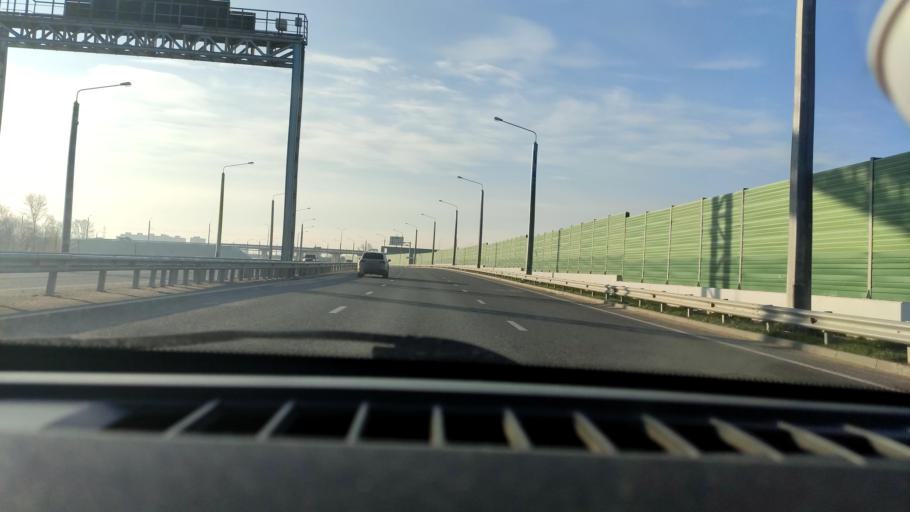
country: RU
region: Samara
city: Samara
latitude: 53.1687
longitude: 50.0855
